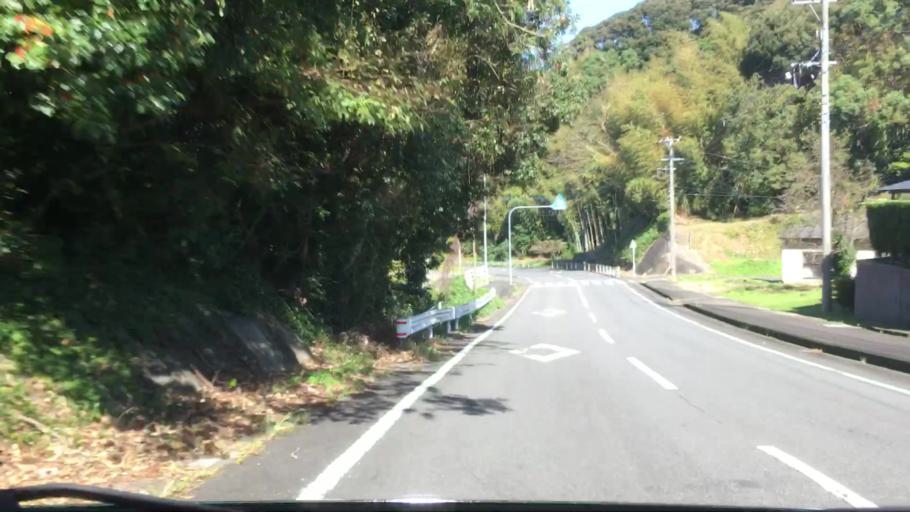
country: JP
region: Nagasaki
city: Sasebo
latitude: 33.0102
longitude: 129.6560
